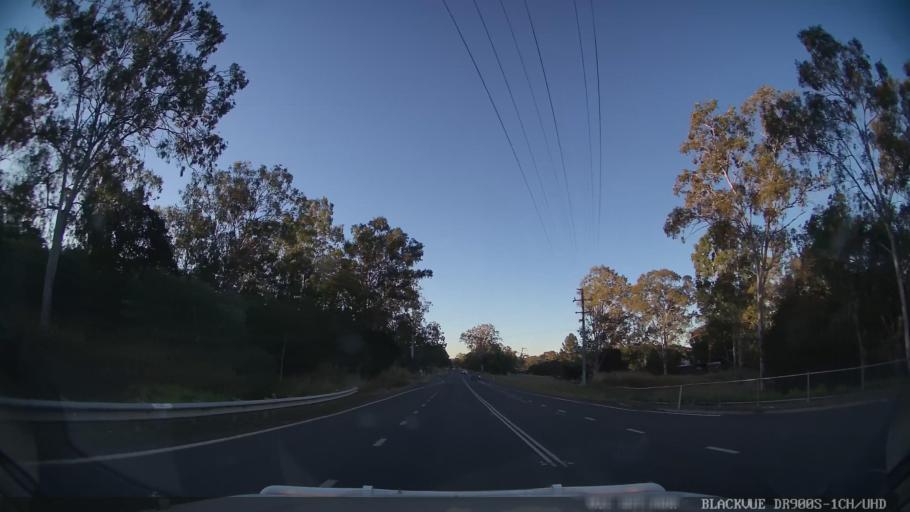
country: AU
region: Queensland
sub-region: Gladstone
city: Toolooa
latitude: -23.9613
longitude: 151.2182
